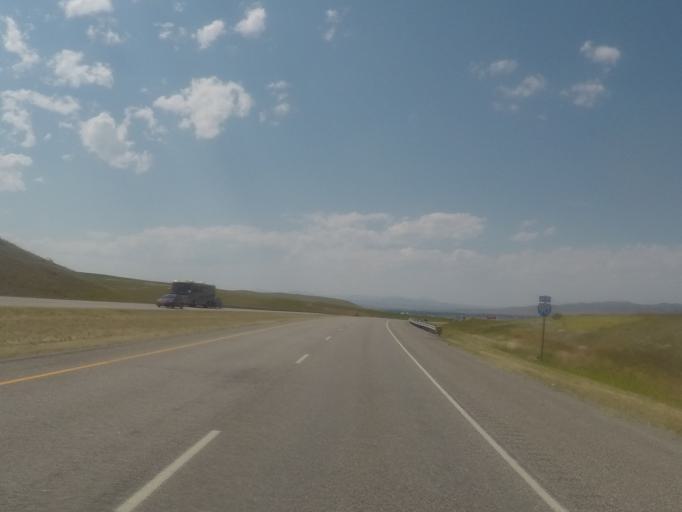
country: US
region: Montana
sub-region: Gallatin County
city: Three Forks
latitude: 45.8830
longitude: -111.4480
